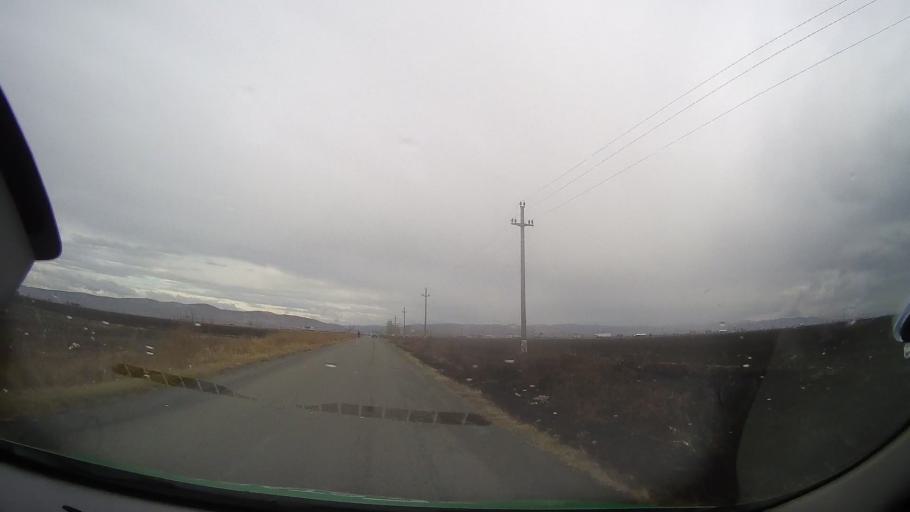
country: RO
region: Prahova
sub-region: Comuna Colceag
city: Inotesti
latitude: 44.9758
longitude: 26.3413
